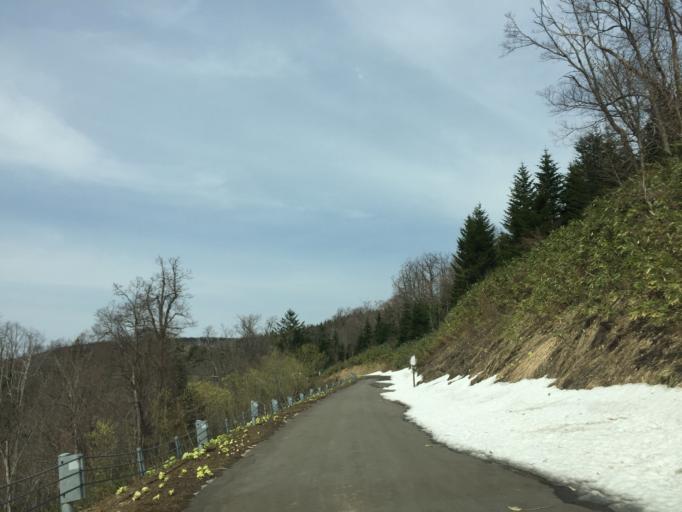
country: JP
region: Hokkaido
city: Akabira
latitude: 43.6055
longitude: 142.0674
